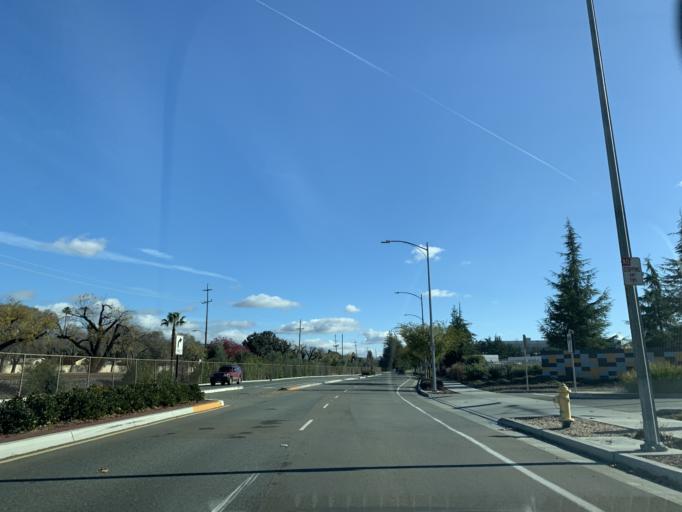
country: US
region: California
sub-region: Santa Clara County
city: Seven Trees
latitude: 37.2509
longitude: -121.7957
